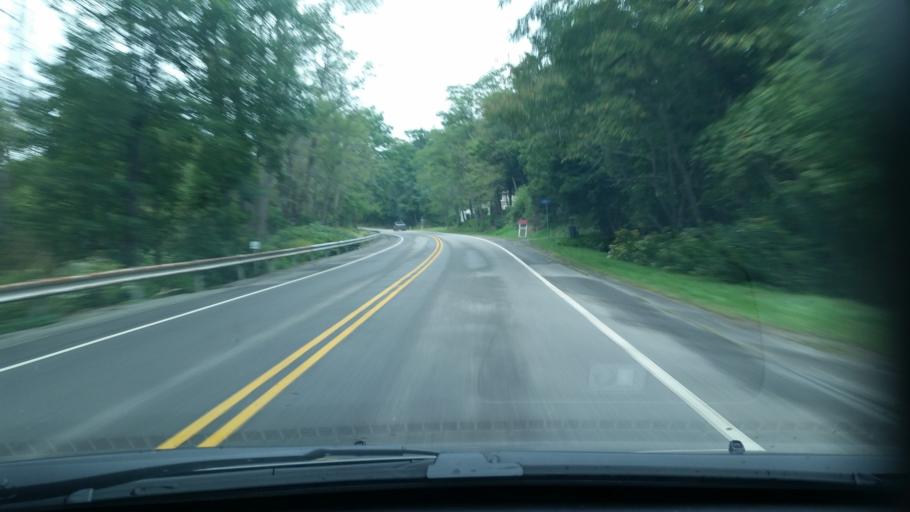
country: US
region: Pennsylvania
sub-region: Clearfield County
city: Shiloh
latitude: 41.0785
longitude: -78.3358
